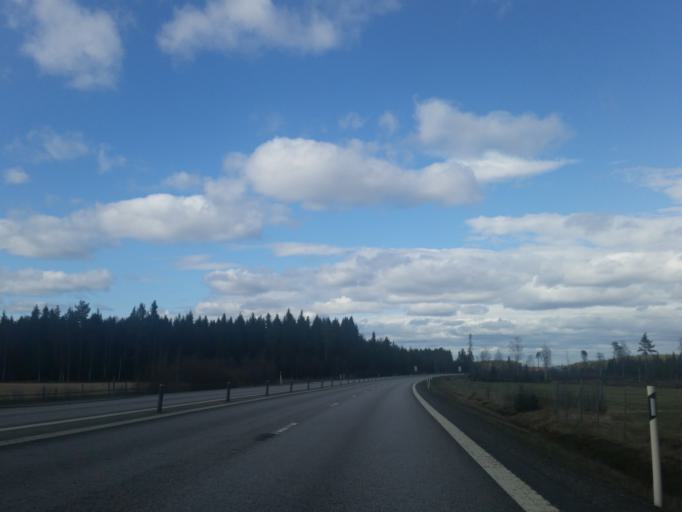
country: SE
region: Vaesterbotten
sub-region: Robertsfors Kommun
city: Robertsfors
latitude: 64.1202
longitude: 20.8821
